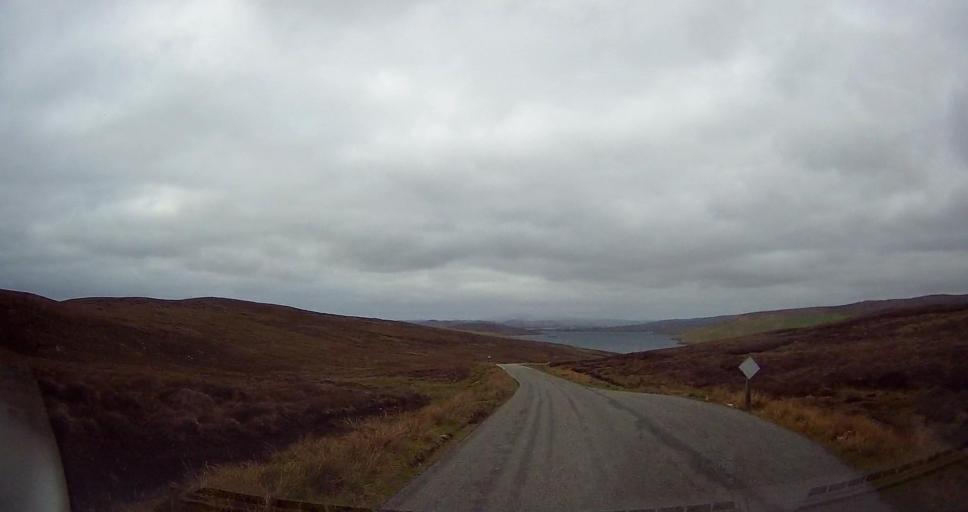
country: GB
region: Scotland
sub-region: Shetland Islands
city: Lerwick
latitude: 60.3228
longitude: -1.3384
